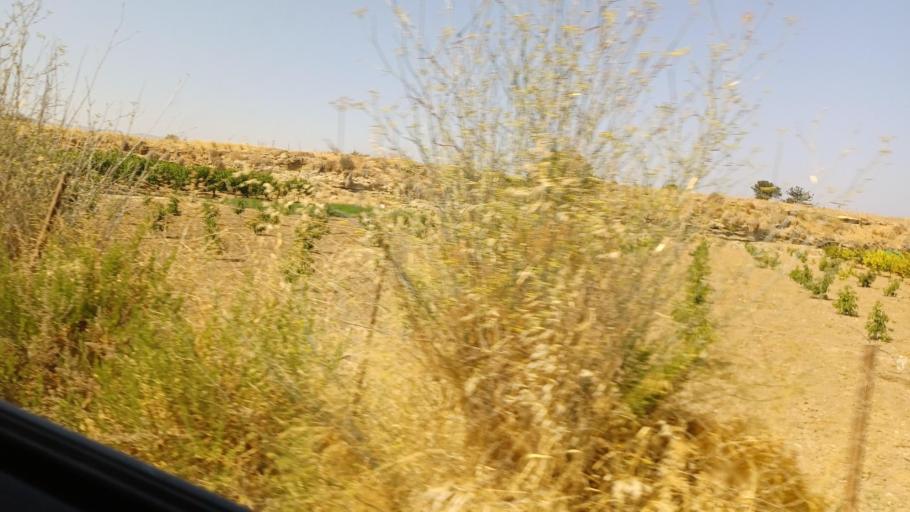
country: CY
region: Pafos
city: Polis
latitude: 35.0477
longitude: 32.4454
